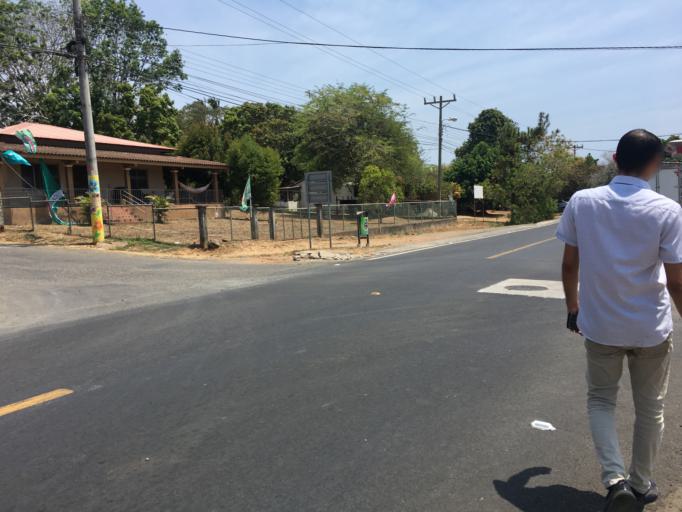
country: PA
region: Los Santos
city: Pedasi
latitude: 7.5330
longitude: -80.0265
